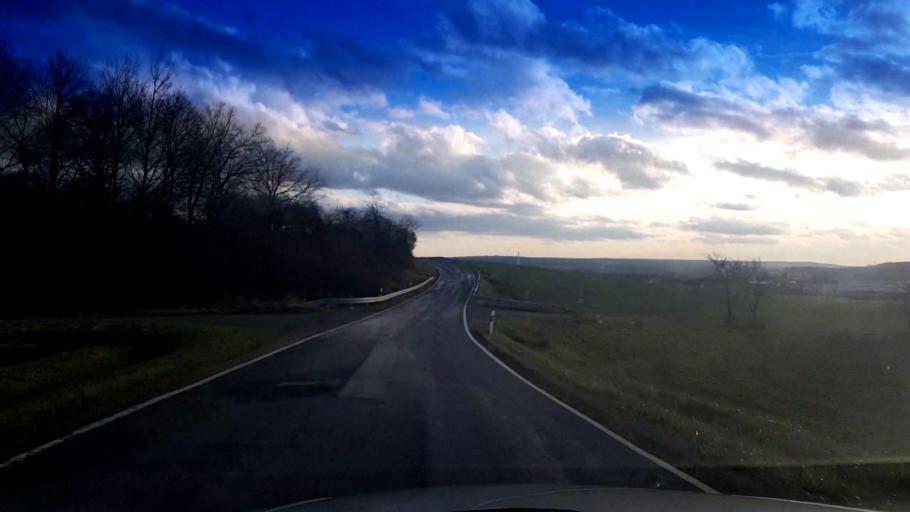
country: DE
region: Bavaria
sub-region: Upper Franconia
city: Buttenheim
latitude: 49.8143
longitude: 11.0267
